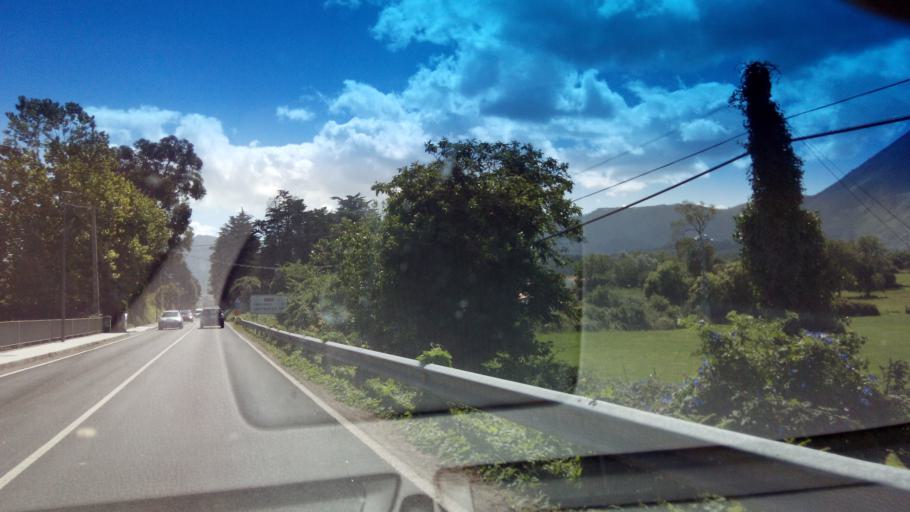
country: ES
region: Asturias
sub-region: Province of Asturias
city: Colunga
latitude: 43.4775
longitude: -5.2258
